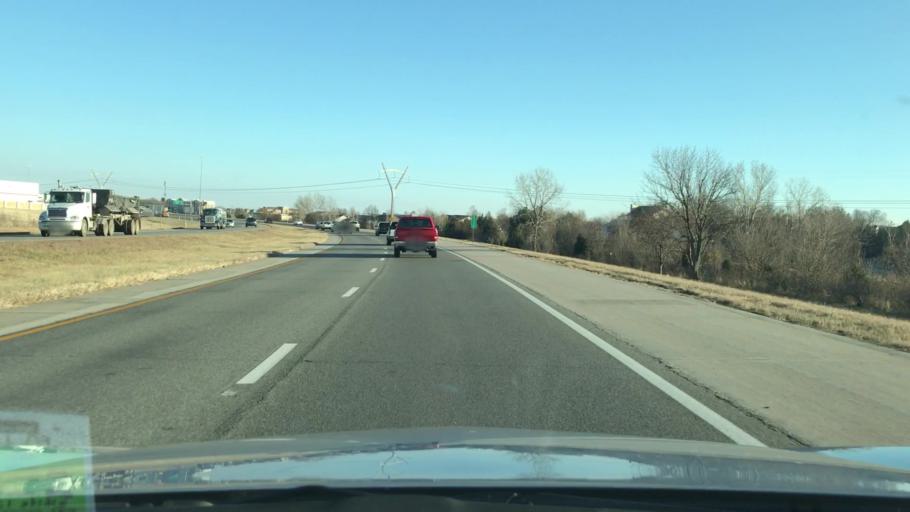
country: US
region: Kansas
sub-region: Sedgwick County
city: Bellaire
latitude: 37.7317
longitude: -97.2189
